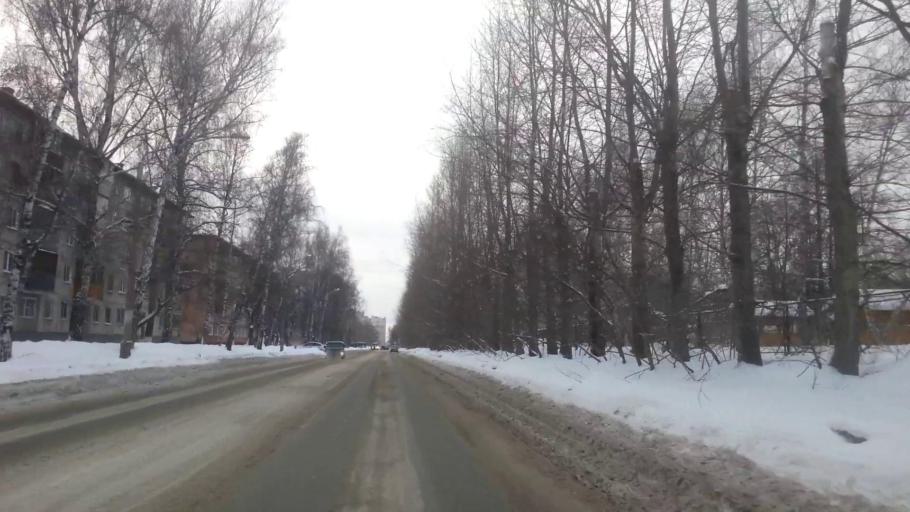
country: RU
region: Altai Krai
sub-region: Gorod Barnaulskiy
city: Barnaul
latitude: 53.3677
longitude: 83.6933
